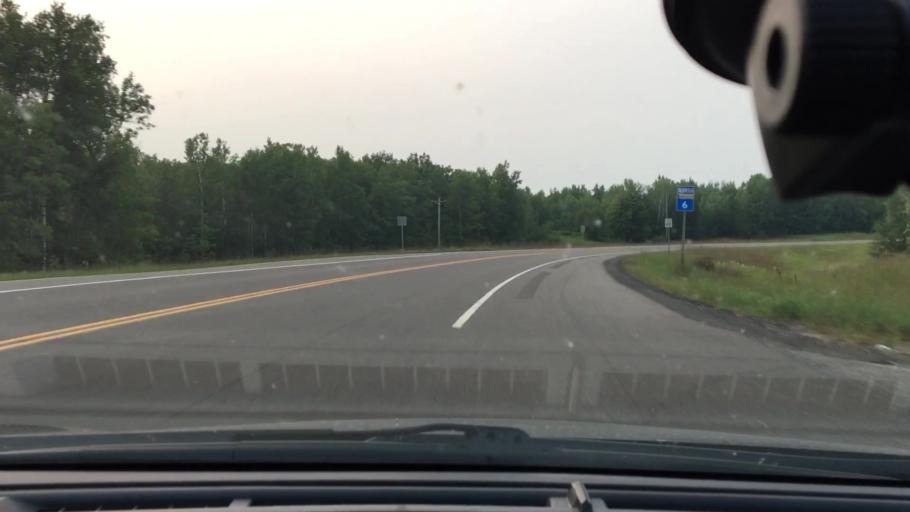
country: US
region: Minnesota
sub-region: Crow Wing County
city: Crosby
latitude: 46.5463
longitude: -93.9581
